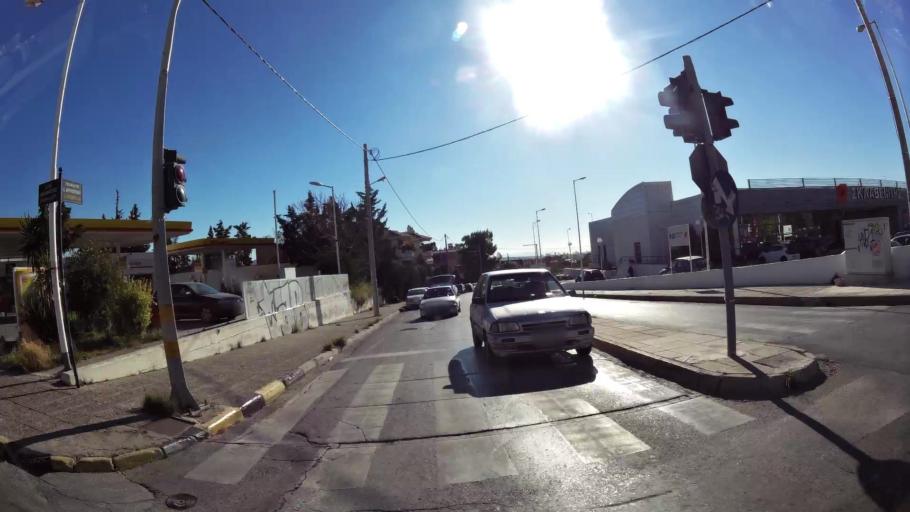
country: GR
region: Attica
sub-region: Nomarchia Athinas
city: Melissia
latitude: 38.0441
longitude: 23.8435
